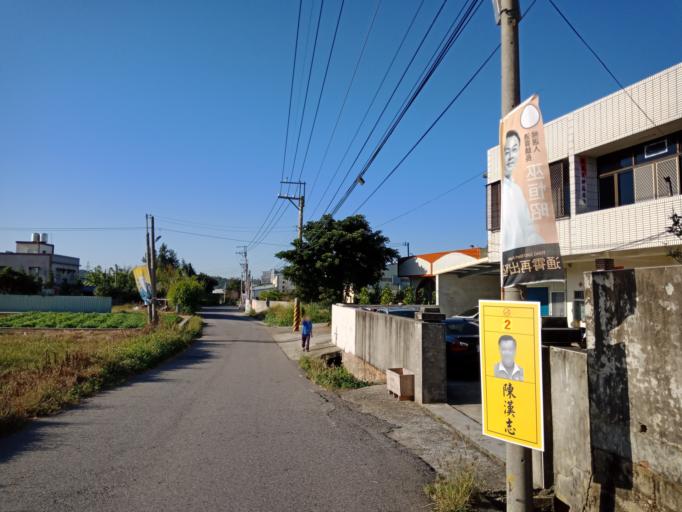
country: TW
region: Taiwan
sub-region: Miaoli
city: Miaoli
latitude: 24.4904
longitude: 120.6969
